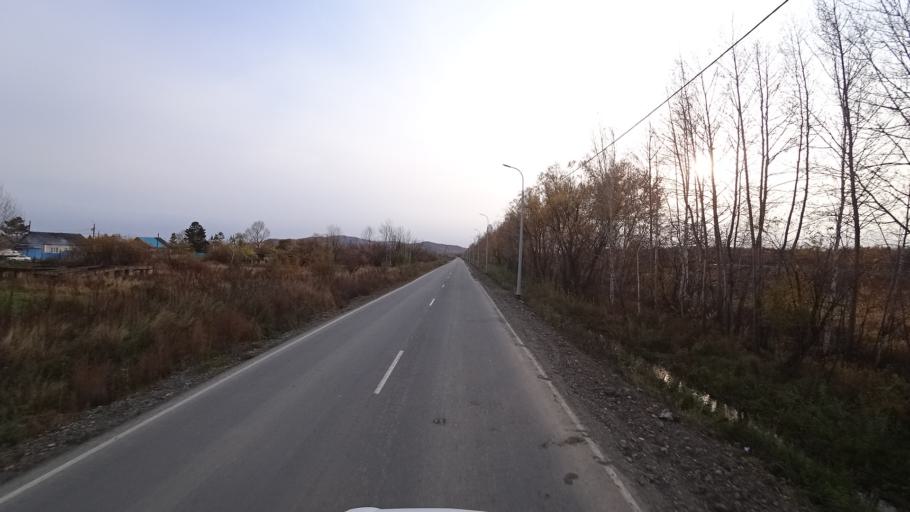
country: RU
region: Khabarovsk Krai
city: Amursk
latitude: 50.0776
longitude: 136.4925
